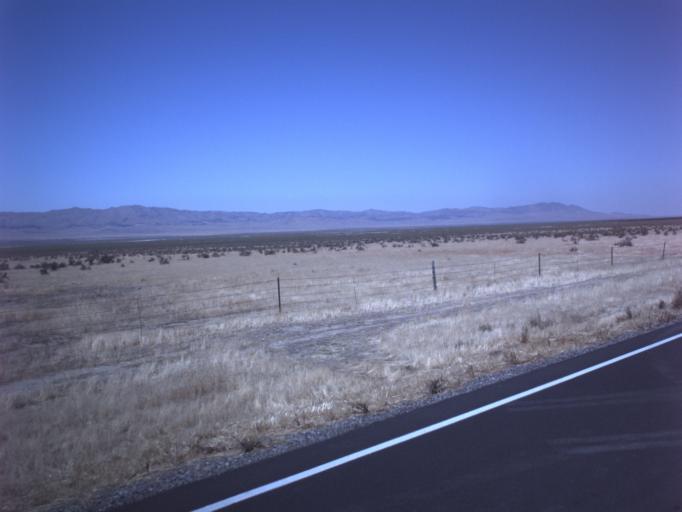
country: US
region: Utah
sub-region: Tooele County
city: Grantsville
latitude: 40.4598
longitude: -112.7474
